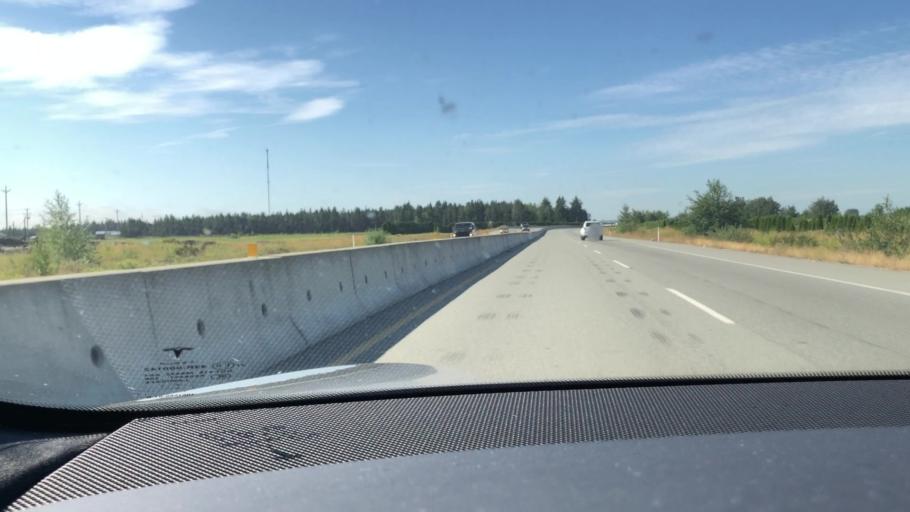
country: CA
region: British Columbia
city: Ladner
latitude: 49.1207
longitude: -123.0256
